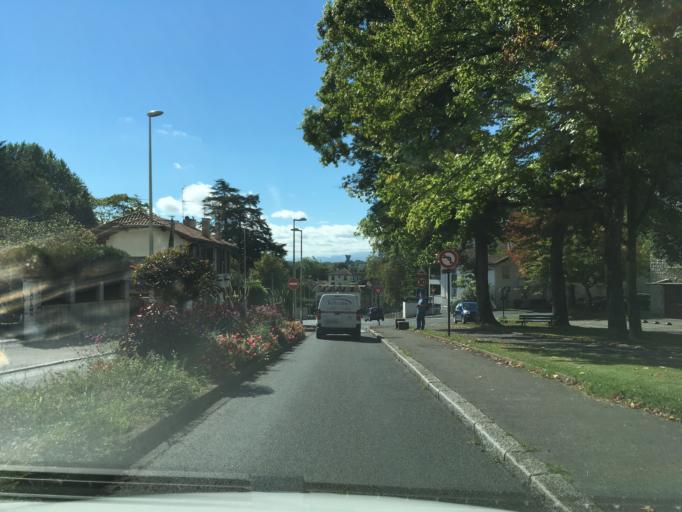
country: FR
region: Aquitaine
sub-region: Departement des Pyrenees-Atlantiques
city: Bayonne
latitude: 43.5016
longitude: -1.4674
